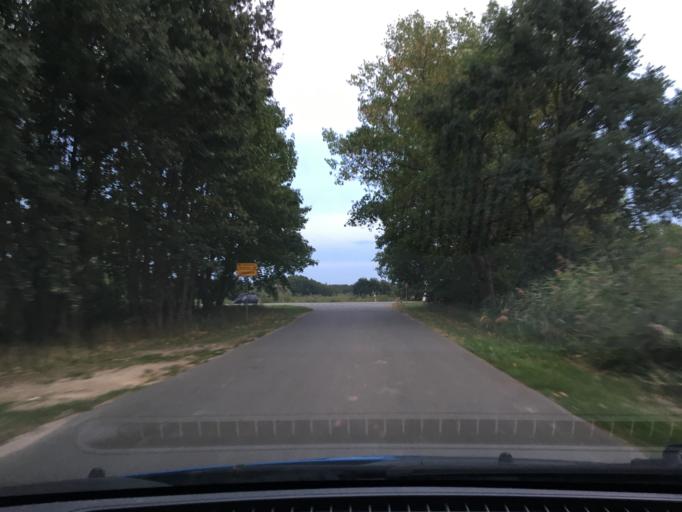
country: DE
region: Lower Saxony
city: Brietlingen
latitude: 53.3473
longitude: 10.4573
